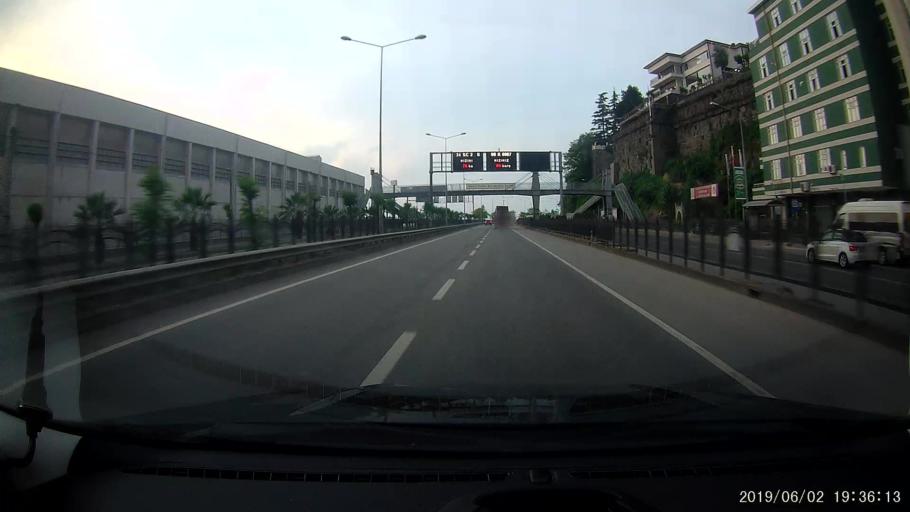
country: TR
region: Giresun
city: Giresun
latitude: 40.9209
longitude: 38.3860
